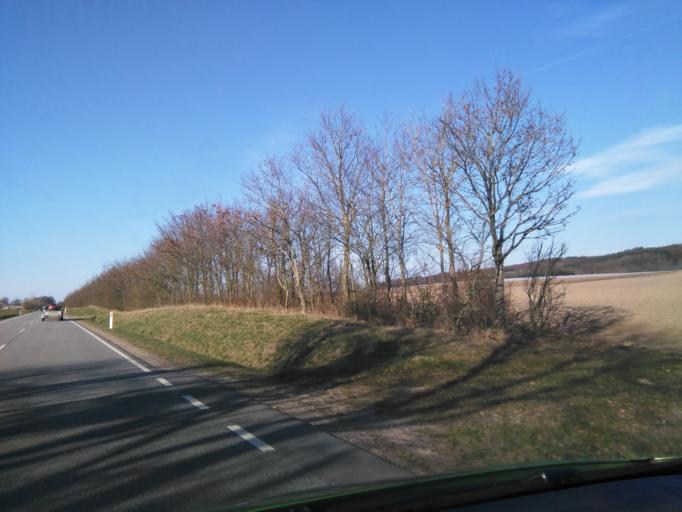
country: DK
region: Central Jutland
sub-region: Skanderborg Kommune
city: Ry
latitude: 55.9928
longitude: 9.7678
